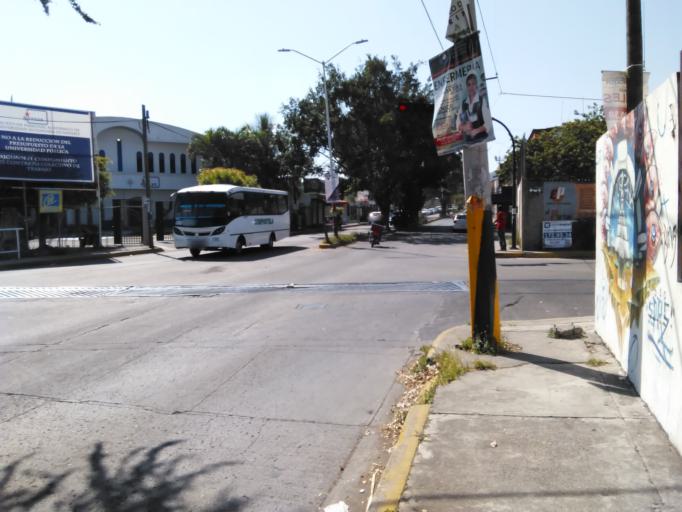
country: MX
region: Nayarit
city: Tepic
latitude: 21.4972
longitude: -104.8929
